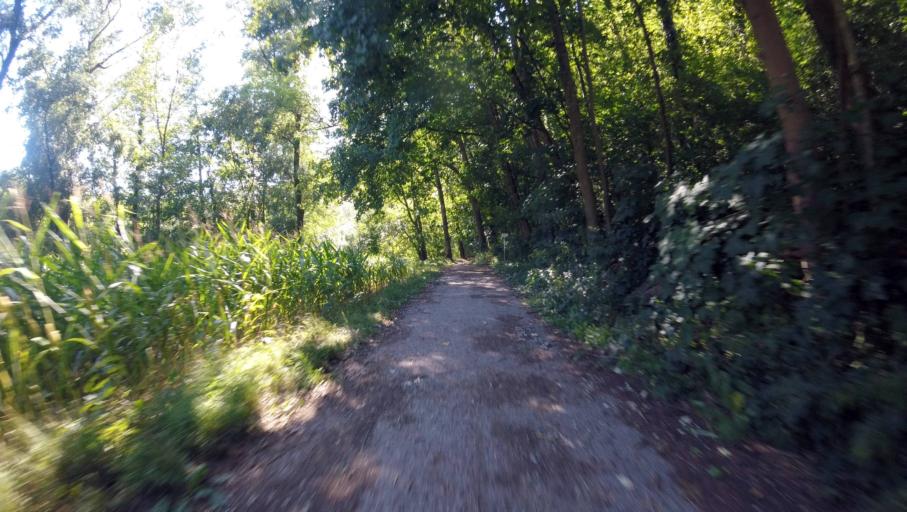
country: DE
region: Baden-Wuerttemberg
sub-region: Regierungsbezirk Stuttgart
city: Kirchberg an der Murr
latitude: 48.9343
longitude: 9.3498
